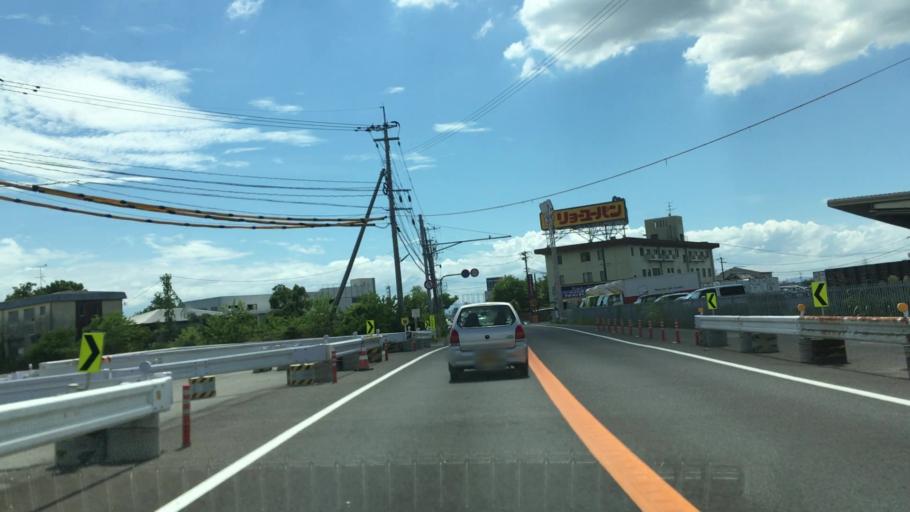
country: JP
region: Saga Prefecture
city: Kanzakimachi-kanzaki
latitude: 33.2855
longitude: 130.3484
